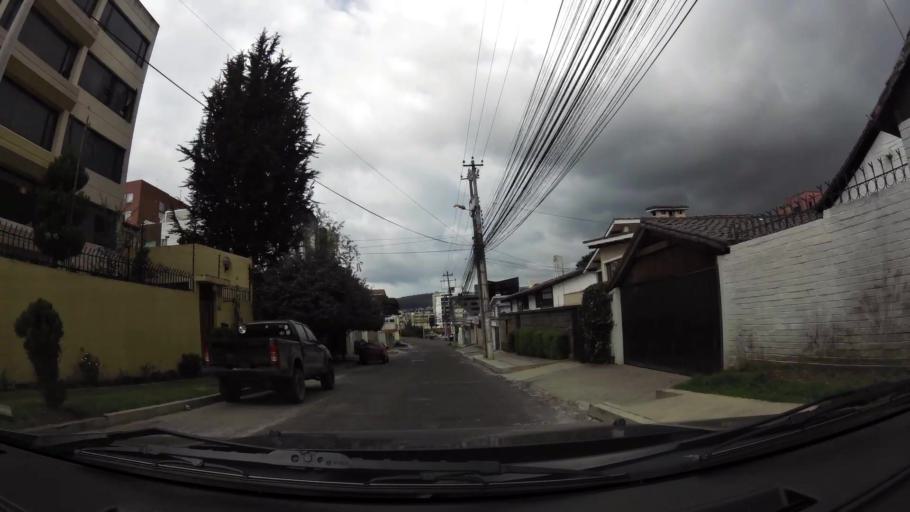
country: EC
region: Pichincha
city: Quito
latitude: -0.1692
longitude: -78.4911
